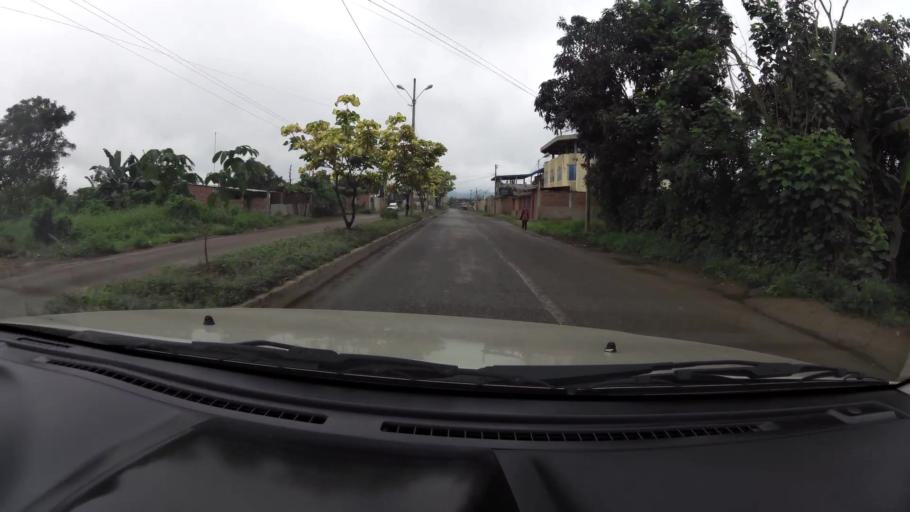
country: EC
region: El Oro
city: Pasaje
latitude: -3.3418
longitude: -79.8051
